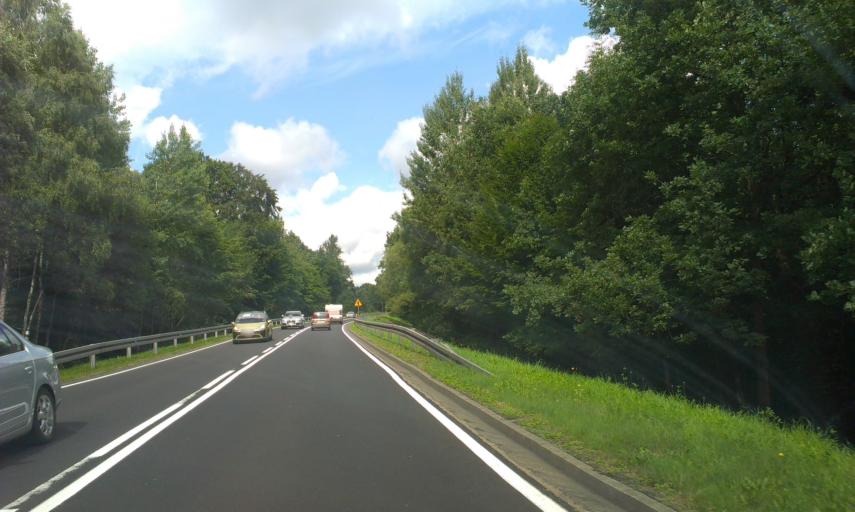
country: PL
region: West Pomeranian Voivodeship
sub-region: Powiat koszalinski
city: Bobolice
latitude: 53.9858
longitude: 16.5401
